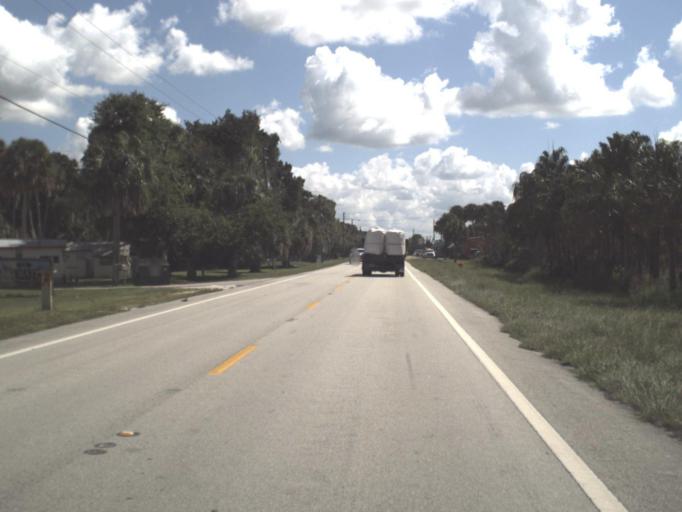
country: US
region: Florida
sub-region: Okeechobee County
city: Taylor Creek
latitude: 27.1588
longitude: -80.7088
